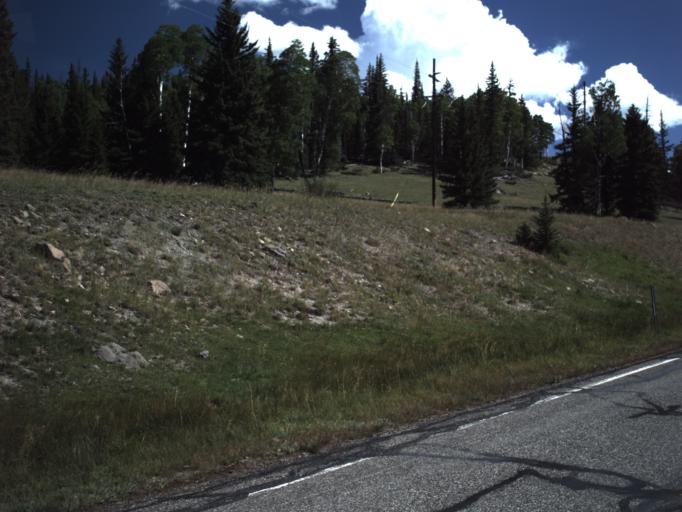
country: US
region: Utah
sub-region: Piute County
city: Junction
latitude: 38.3050
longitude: -112.4206
